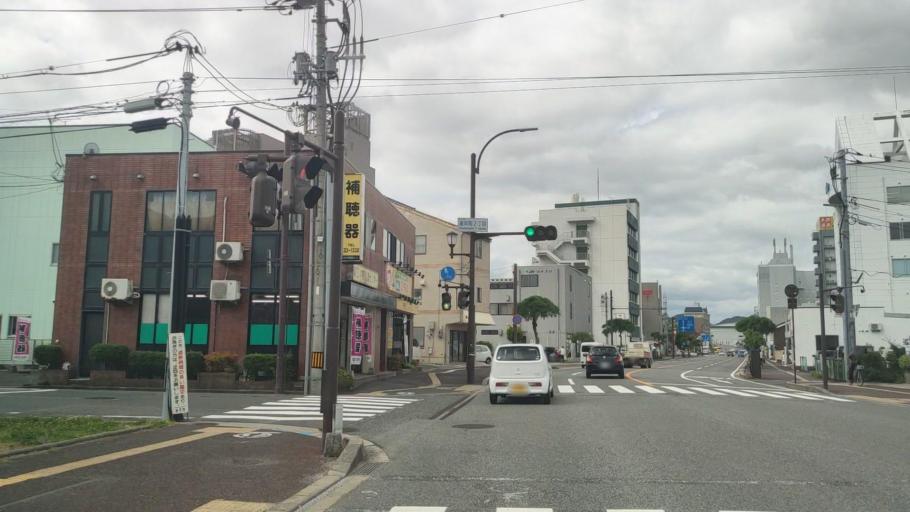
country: JP
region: Tottori
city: Yonago
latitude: 35.4263
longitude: 133.3377
